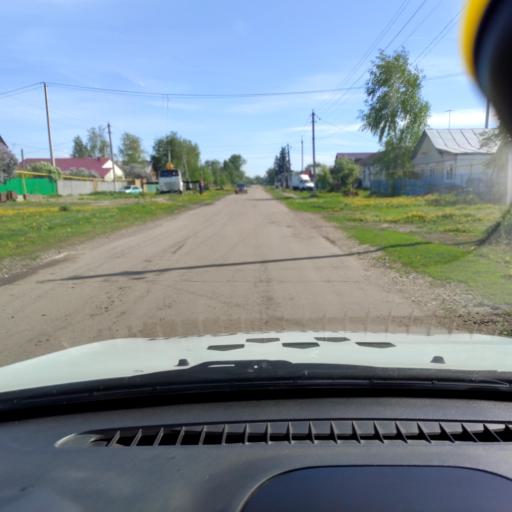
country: RU
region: Samara
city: Tol'yatti
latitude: 53.6719
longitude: 49.4306
